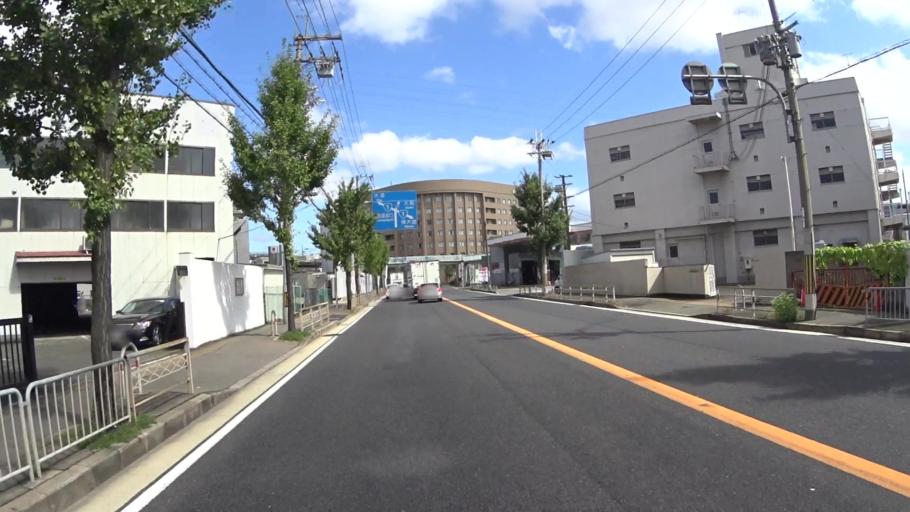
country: JP
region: Kyoto
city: Muko
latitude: 34.9317
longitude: 135.7437
